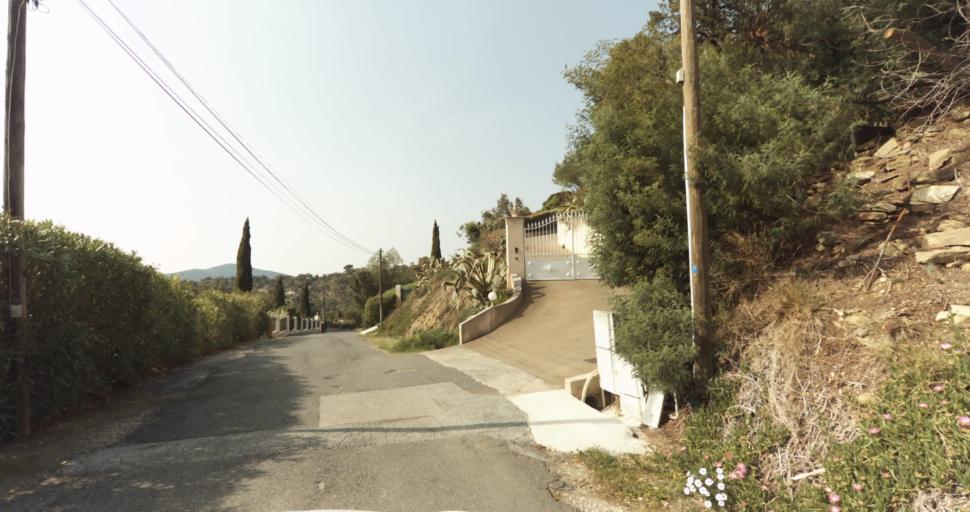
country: FR
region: Provence-Alpes-Cote d'Azur
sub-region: Departement du Var
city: Bormes-les-Mimosas
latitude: 43.1482
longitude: 6.3284
